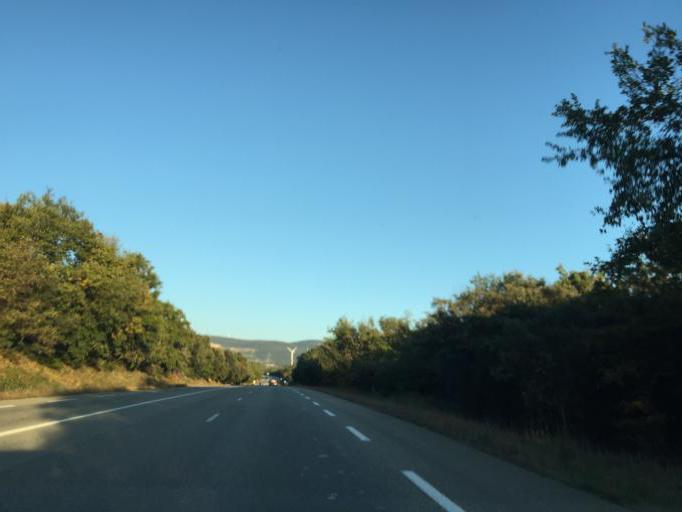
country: FR
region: Rhone-Alpes
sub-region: Departement de la Drome
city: Donzere
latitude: 44.4472
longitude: 4.7316
